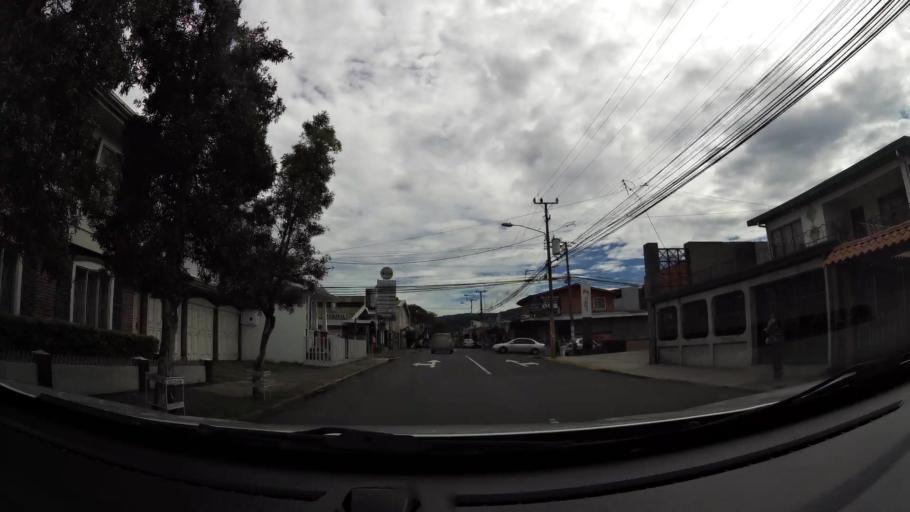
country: CR
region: San Jose
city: San Rafael Arriba
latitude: 9.8987
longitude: -84.0672
